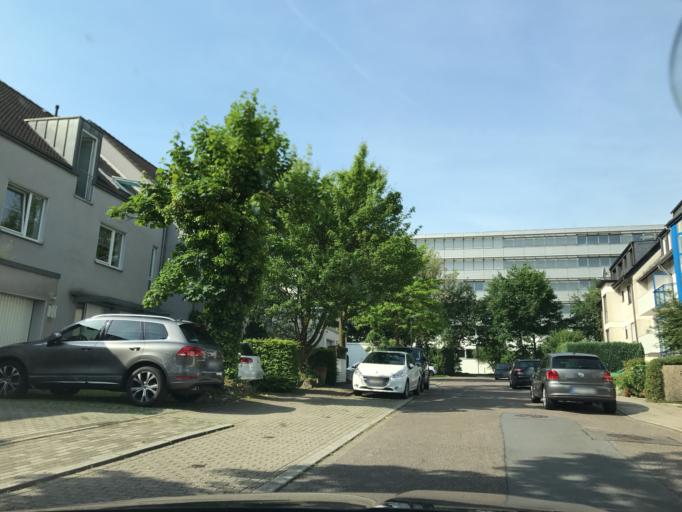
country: DE
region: North Rhine-Westphalia
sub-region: Regierungsbezirk Dusseldorf
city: Essen
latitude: 51.4153
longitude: 6.9811
